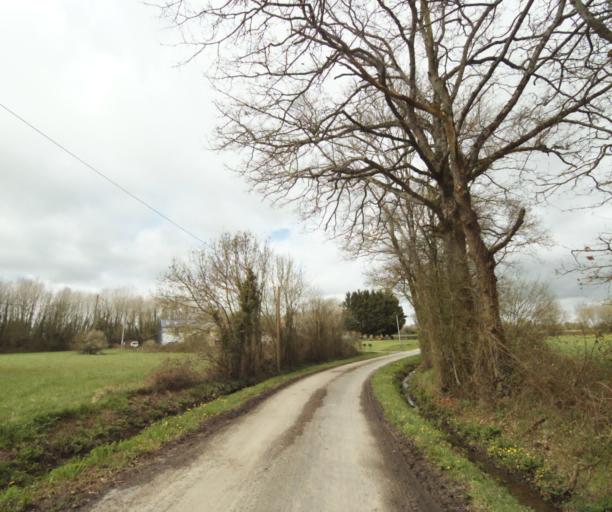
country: FR
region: Pays de la Loire
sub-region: Departement de la Loire-Atlantique
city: Bouvron
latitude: 47.4365
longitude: -1.8457
